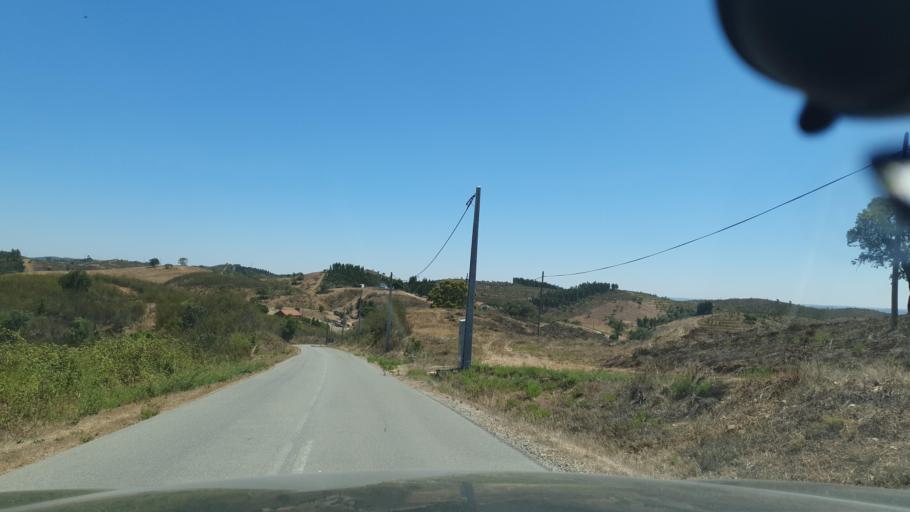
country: PT
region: Beja
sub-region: Ourique
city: Ourique
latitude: 37.5538
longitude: -8.4094
